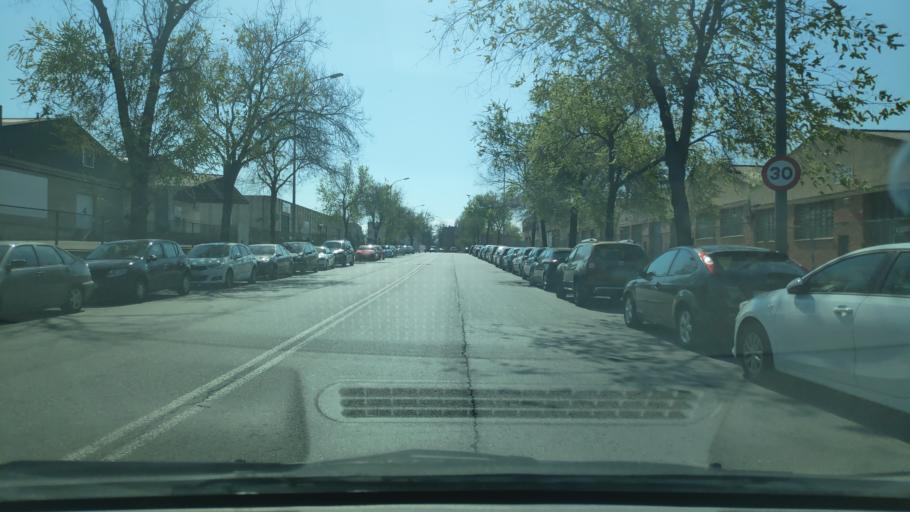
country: ES
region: Catalonia
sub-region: Provincia de Barcelona
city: Sabadell
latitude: 41.5440
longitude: 2.1296
